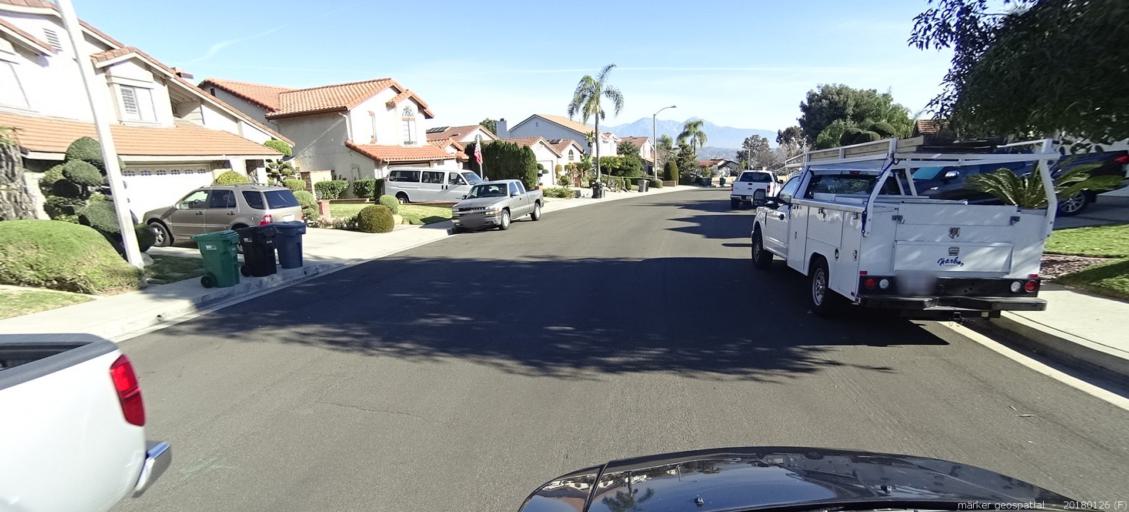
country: US
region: California
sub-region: Los Angeles County
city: Walnut
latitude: 33.9850
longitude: -117.8523
